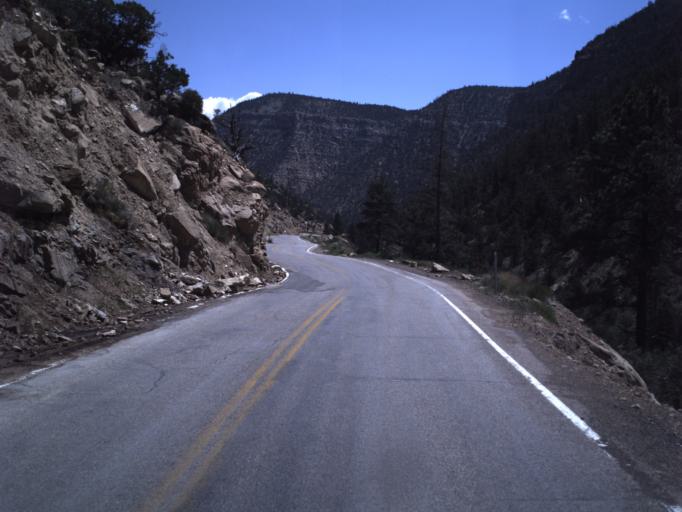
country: US
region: Utah
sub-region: Emery County
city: Orangeville
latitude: 39.2866
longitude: -111.2388
